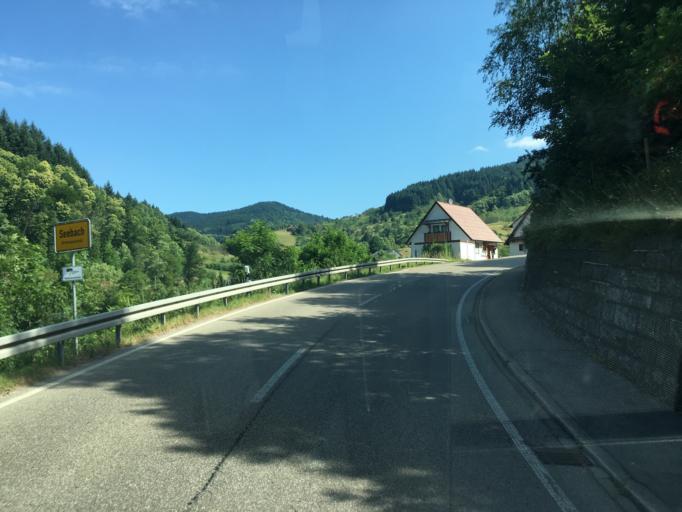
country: DE
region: Baden-Wuerttemberg
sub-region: Freiburg Region
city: Seebach
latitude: 48.5743
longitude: 8.1651
